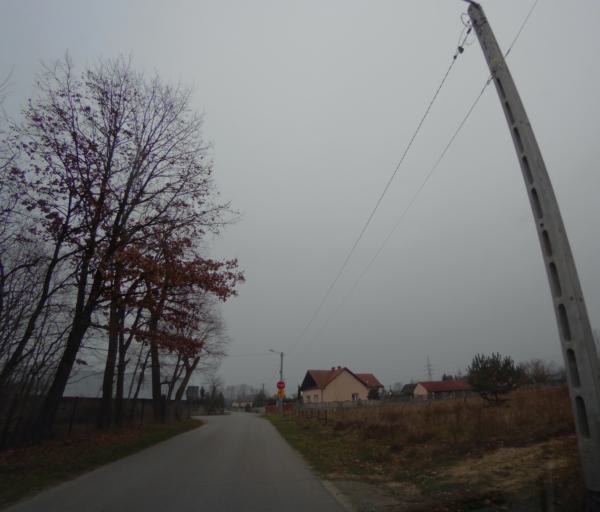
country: PL
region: Subcarpathian Voivodeship
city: Nowa Sarzyna
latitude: 50.2907
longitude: 22.3526
